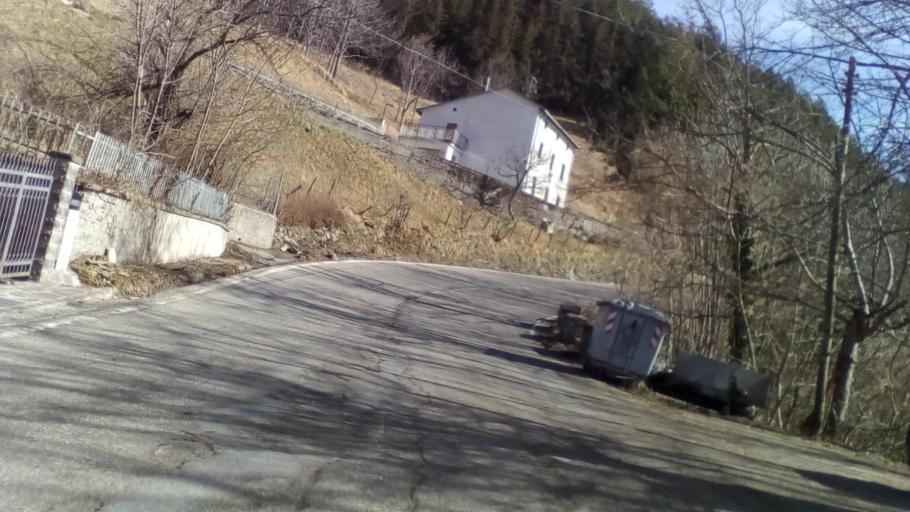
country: IT
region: Emilia-Romagna
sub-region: Provincia di Modena
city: Riolunato
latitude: 44.2575
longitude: 10.6451
